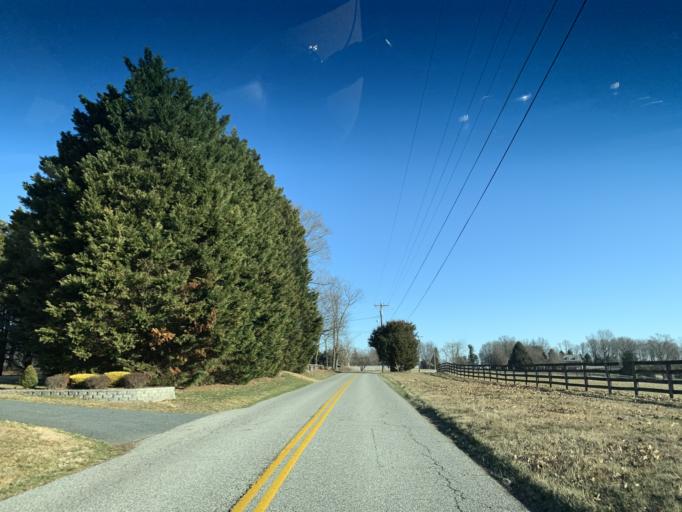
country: US
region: Maryland
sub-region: Harford County
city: Aberdeen
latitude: 39.5719
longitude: -76.2378
